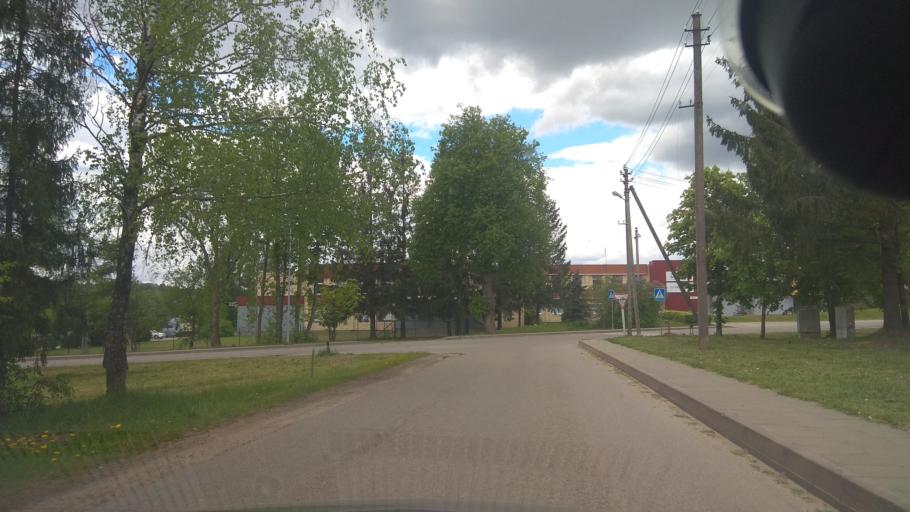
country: LT
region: Vilnius County
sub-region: Vilnius
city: Fabijoniskes
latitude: 54.8045
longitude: 25.2587
